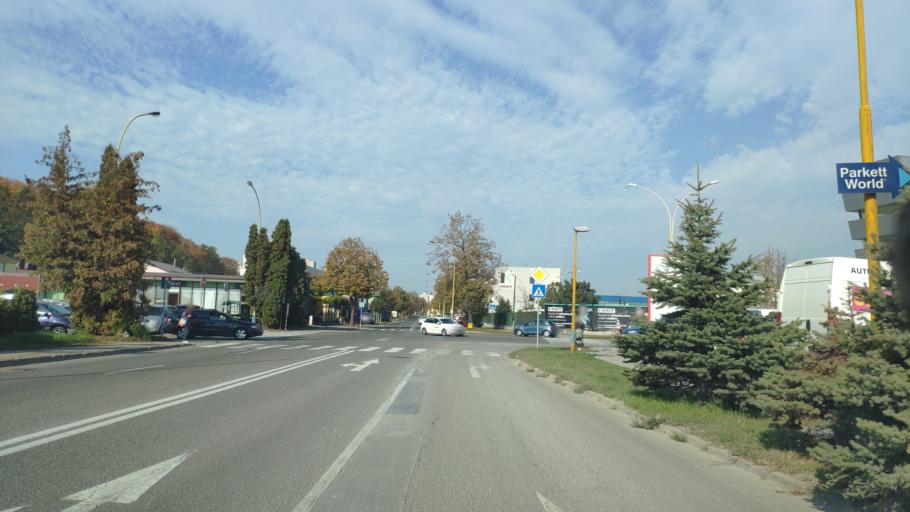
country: SK
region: Kosicky
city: Kosice
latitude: 48.6942
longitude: 21.2622
